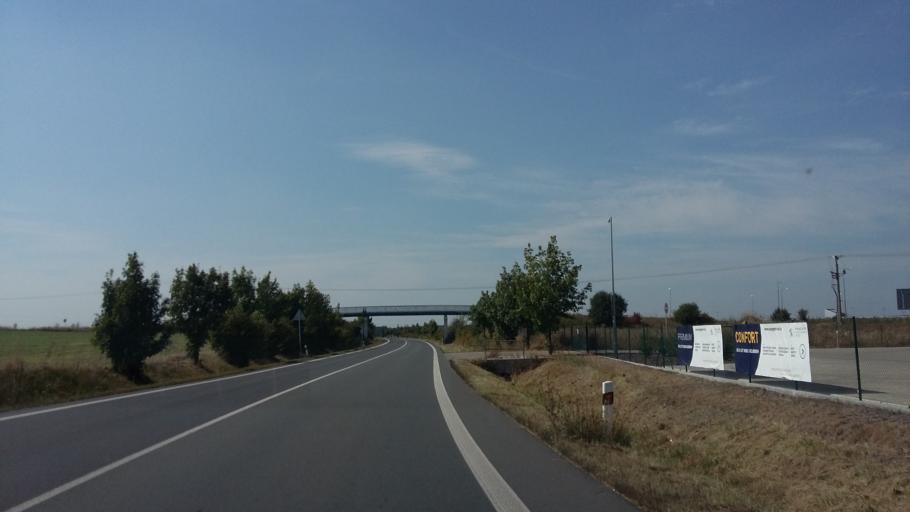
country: CZ
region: Central Bohemia
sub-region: Okres Kolin
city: Kolin
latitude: 50.0590
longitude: 15.2273
